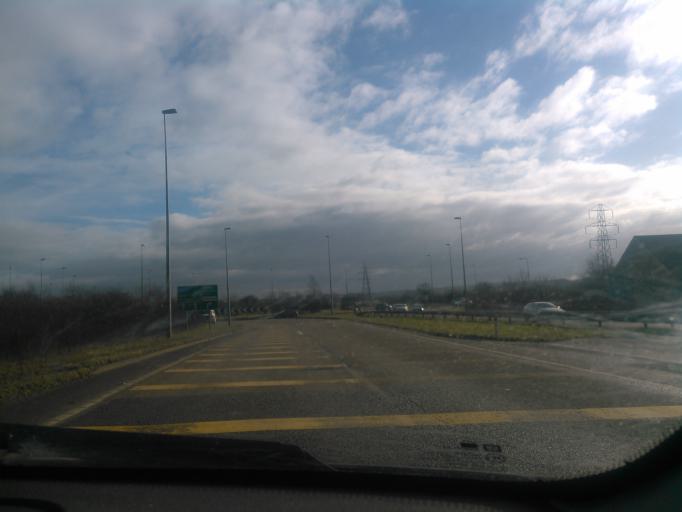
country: GB
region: England
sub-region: Staffordshire
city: Uttoxeter
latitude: 52.9082
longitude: -1.8547
